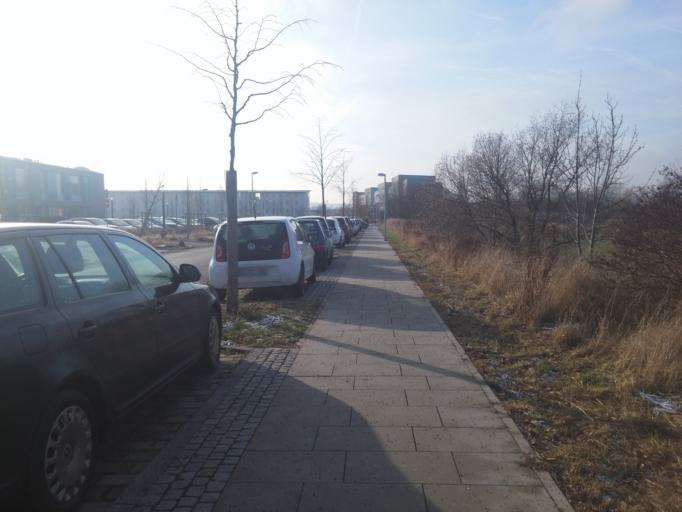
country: DE
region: Bavaria
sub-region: Upper Franconia
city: Coburg
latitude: 50.2805
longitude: 10.9696
